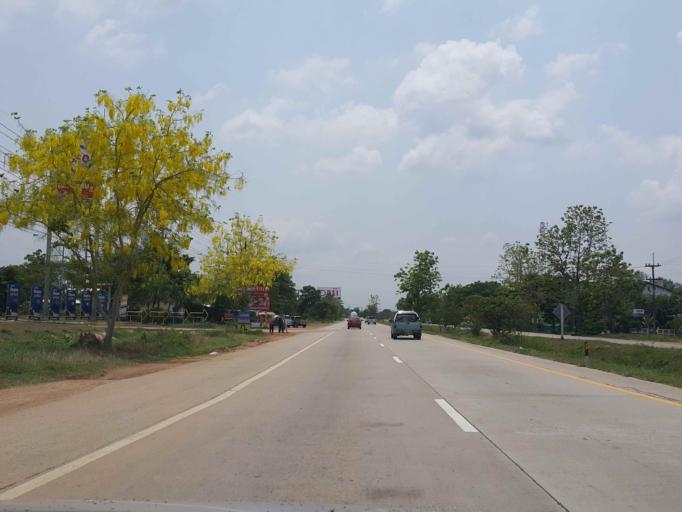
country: TH
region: Lampang
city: Ko Kha
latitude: 18.2188
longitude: 99.4243
